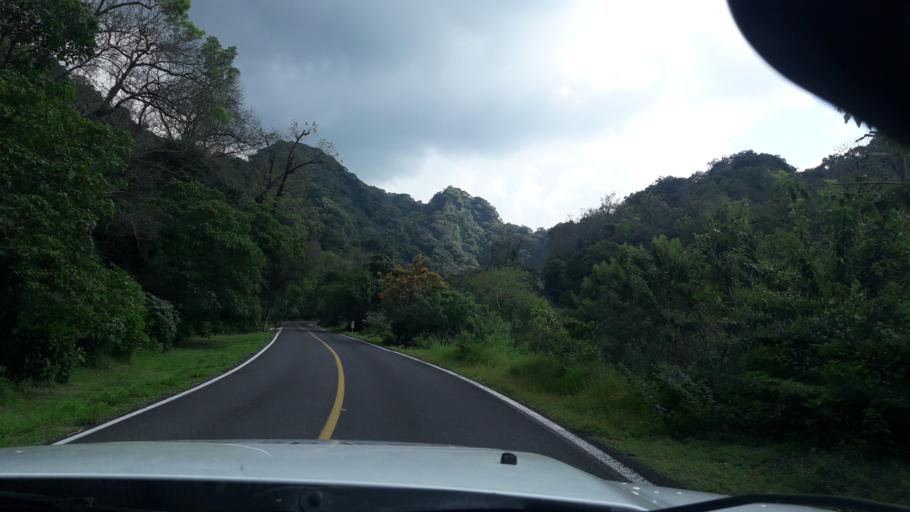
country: MX
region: Colima
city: Suchitlan
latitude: 19.4460
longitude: -103.7175
